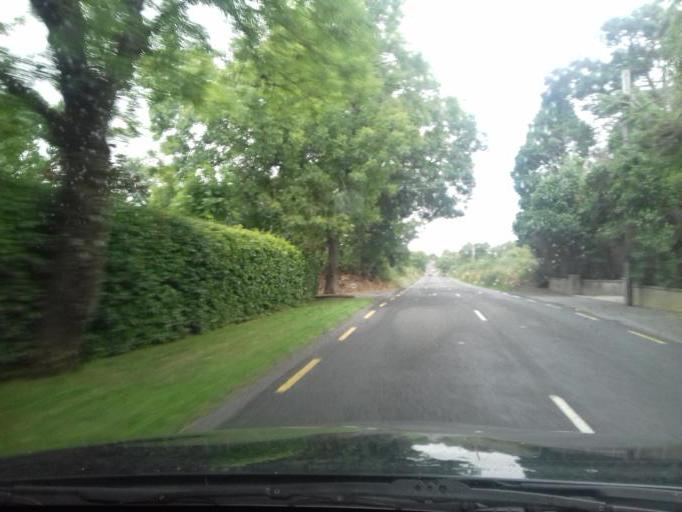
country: IE
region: Leinster
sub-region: County Carlow
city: Bagenalstown
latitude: 52.6217
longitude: -6.9397
